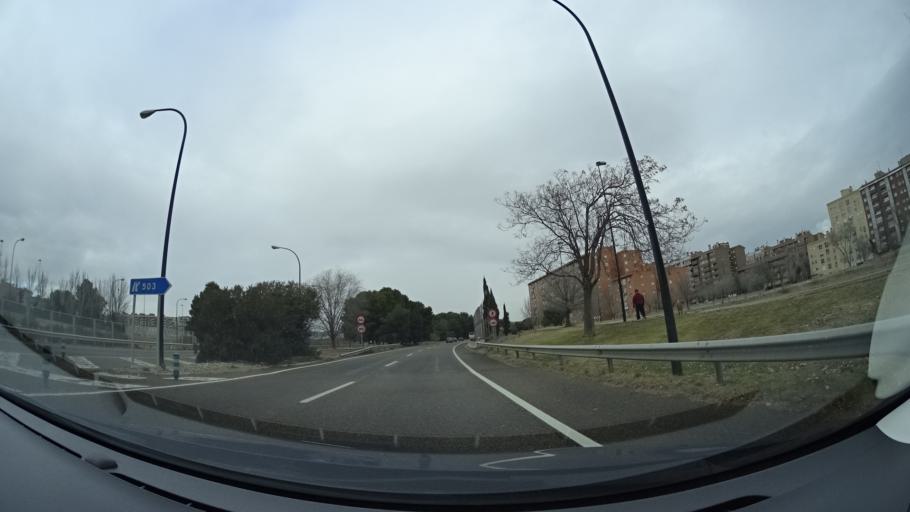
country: ES
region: Aragon
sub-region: Provincia de Zaragoza
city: Zaragoza
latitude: 41.6732
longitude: -0.8803
